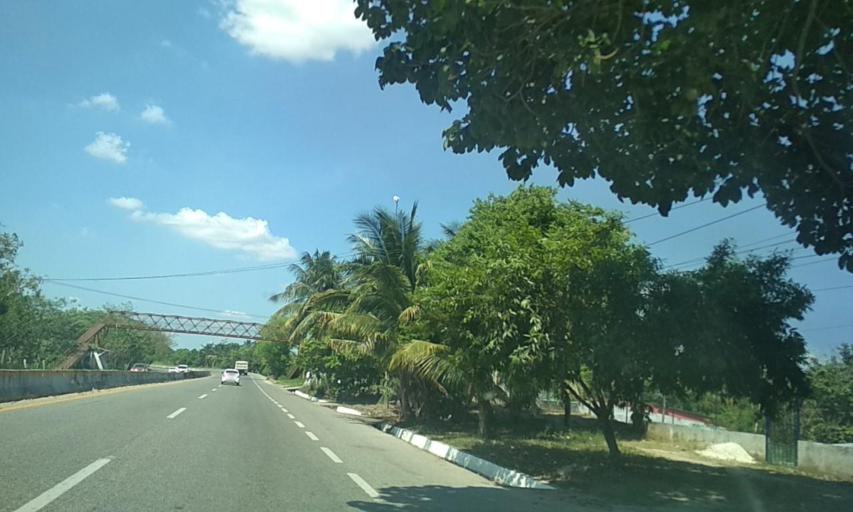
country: MX
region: Tabasco
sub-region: Huimanguillo
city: El Dorado
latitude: 17.8833
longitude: -93.3685
